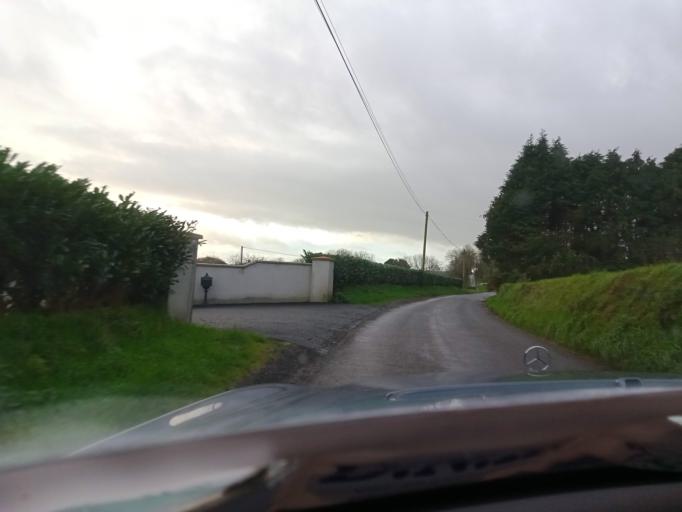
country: IE
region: Leinster
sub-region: Kilkenny
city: Mooncoin
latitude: 52.2694
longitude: -7.1862
